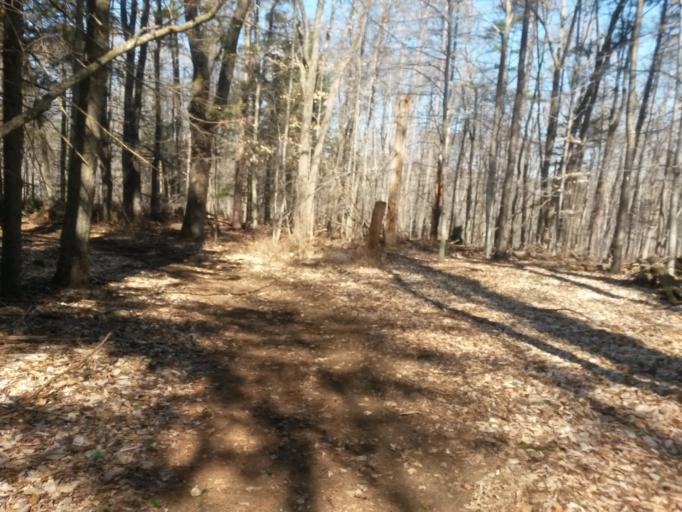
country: US
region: New York
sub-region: Westchester County
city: Yorktown Heights
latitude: 41.2795
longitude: -73.7354
